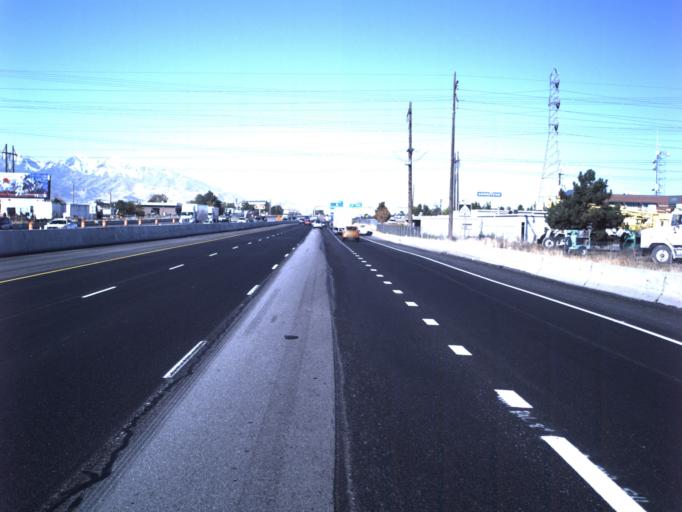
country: US
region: Utah
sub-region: Salt Lake County
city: West Valley City
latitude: 40.7259
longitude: -111.9568
